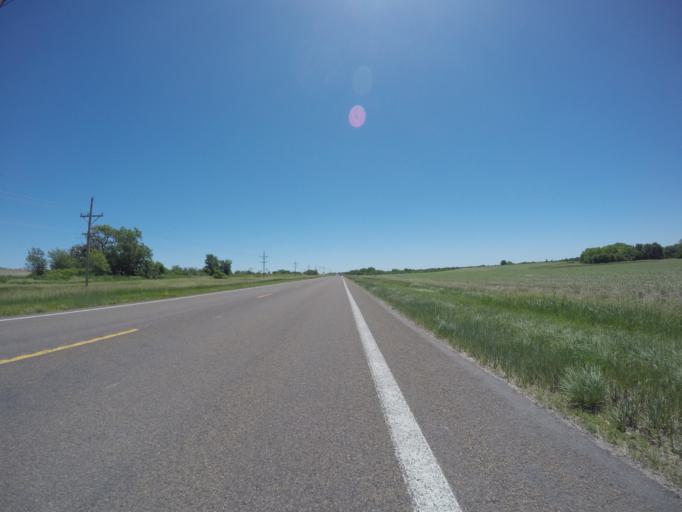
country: US
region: Kansas
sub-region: Phillips County
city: Phillipsburg
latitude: 39.8207
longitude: -99.5396
